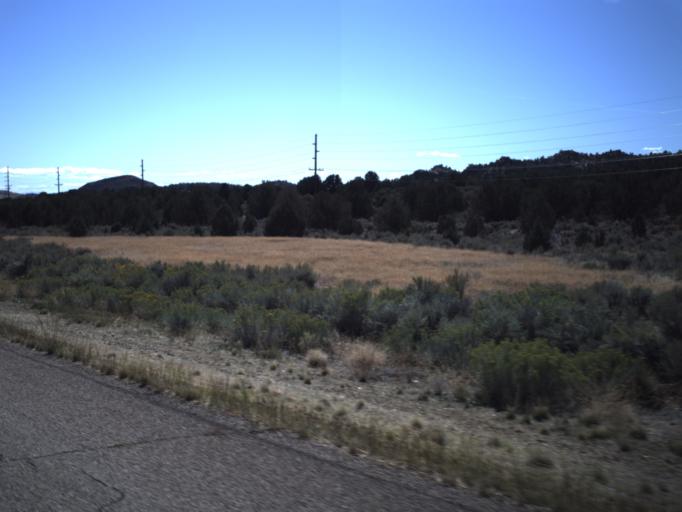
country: US
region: Utah
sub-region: Washington County
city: Ivins
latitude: 37.2717
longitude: -113.6421
